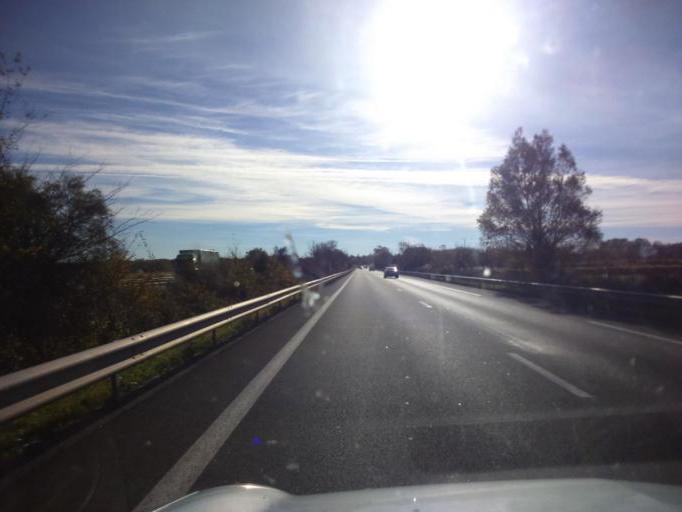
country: FR
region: Poitou-Charentes
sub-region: Departement de la Charente-Maritime
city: Breuil-Magne
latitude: 45.9756
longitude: -0.9923
